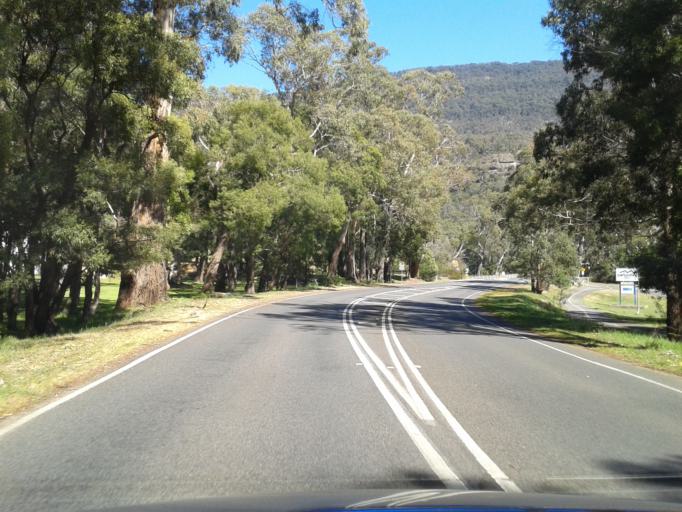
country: AU
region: Victoria
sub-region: Northern Grampians
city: Stawell
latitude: -37.1301
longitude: 142.5247
